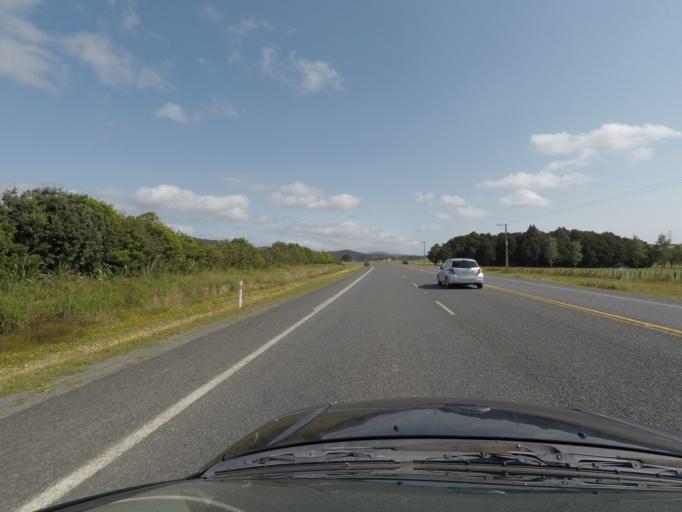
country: NZ
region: Northland
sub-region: Whangarei
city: Ruakaka
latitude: -36.0118
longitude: 174.4180
